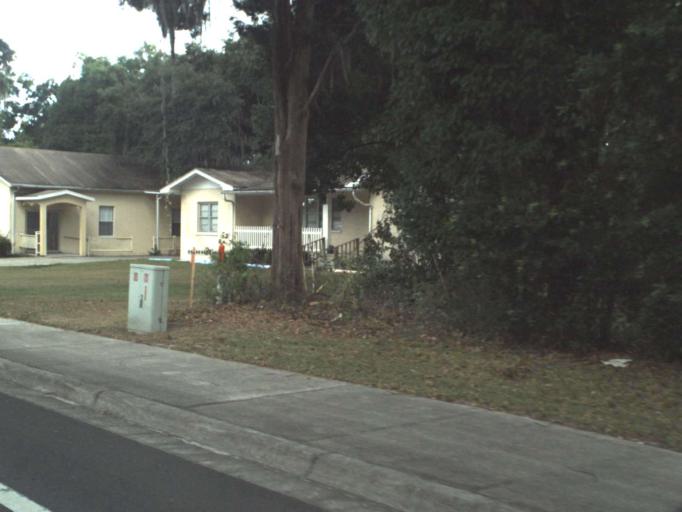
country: US
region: Florida
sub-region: Sumter County
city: Wildwood
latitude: 28.9300
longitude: -82.0372
